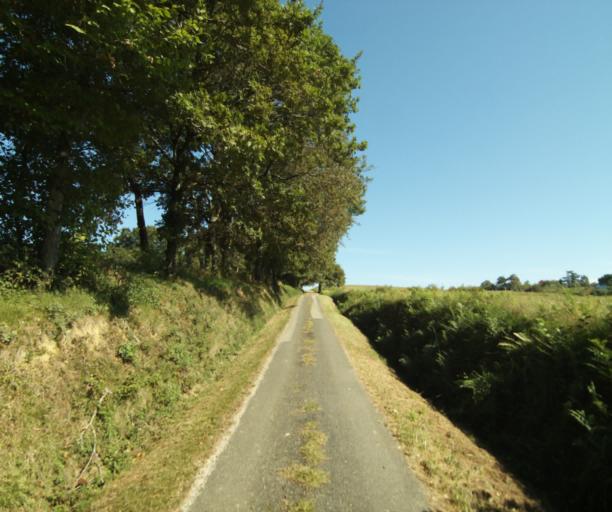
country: FR
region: Aquitaine
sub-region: Departement des Landes
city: Gabarret
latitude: 43.9473
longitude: -0.0010
